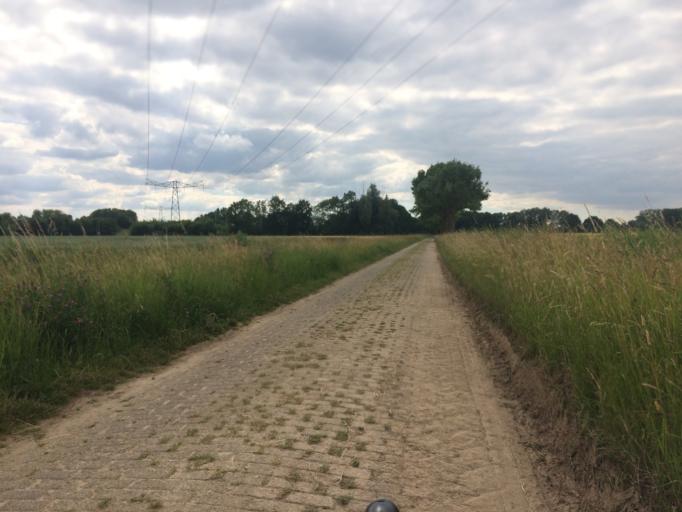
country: NL
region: Gelderland
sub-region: Gemeente Zaltbommel
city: Nederhemert-Noord
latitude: 51.7165
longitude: 5.1974
